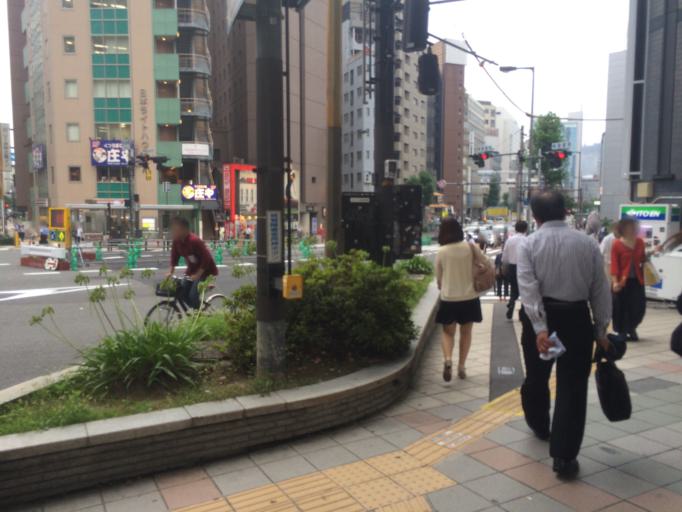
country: JP
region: Osaka
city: Osaka-shi
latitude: 34.6926
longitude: 135.4965
